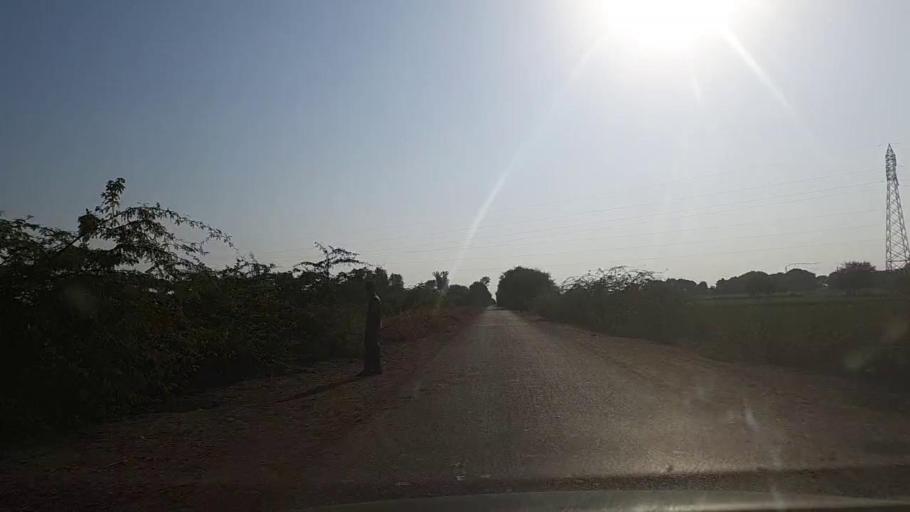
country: PK
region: Sindh
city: Naukot
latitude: 24.9985
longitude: 69.2659
